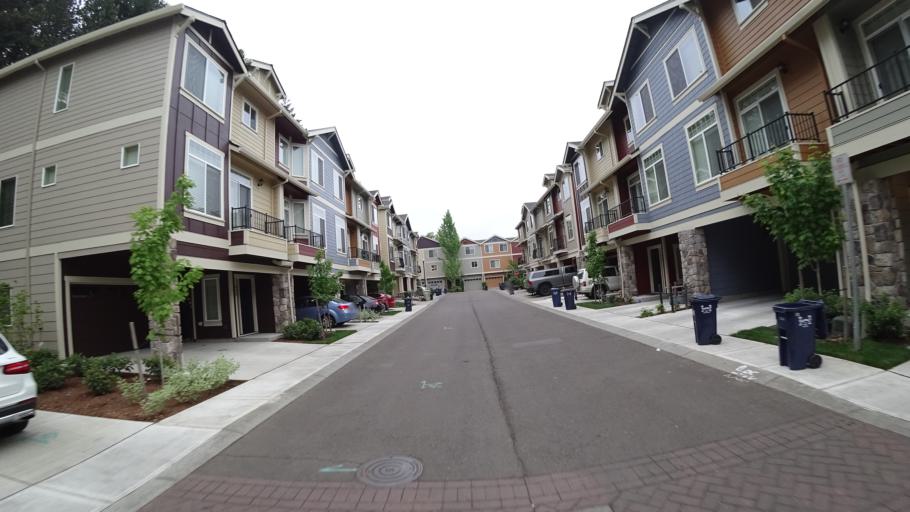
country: US
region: Oregon
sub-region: Washington County
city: Rockcreek
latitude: 45.5240
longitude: -122.8934
